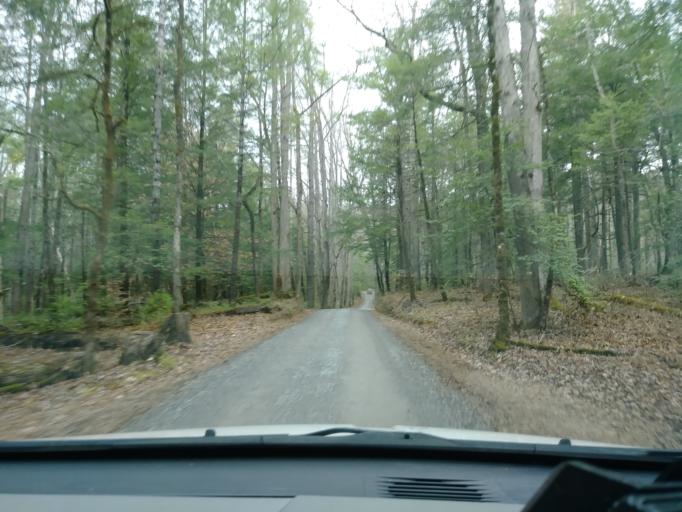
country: US
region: Tennessee
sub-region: Blount County
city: Wildwood
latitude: 35.6045
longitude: -83.8119
